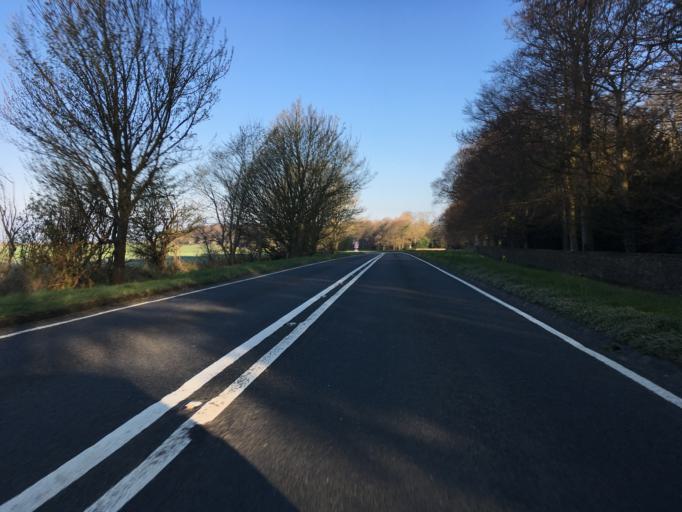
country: GB
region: England
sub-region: Gloucestershire
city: Bourton on the Water
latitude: 51.8207
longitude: -1.7628
